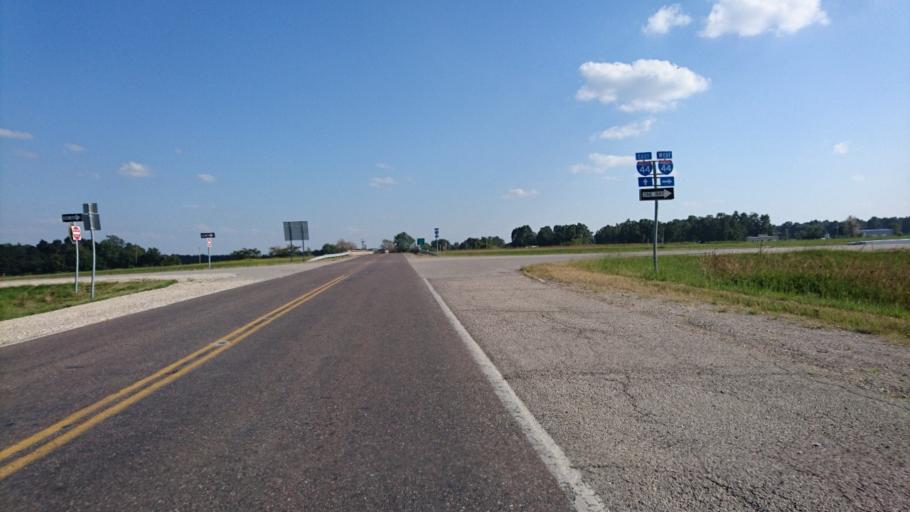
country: US
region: Missouri
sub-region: Laclede County
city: Lebanon
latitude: 37.6006
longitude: -92.7162
